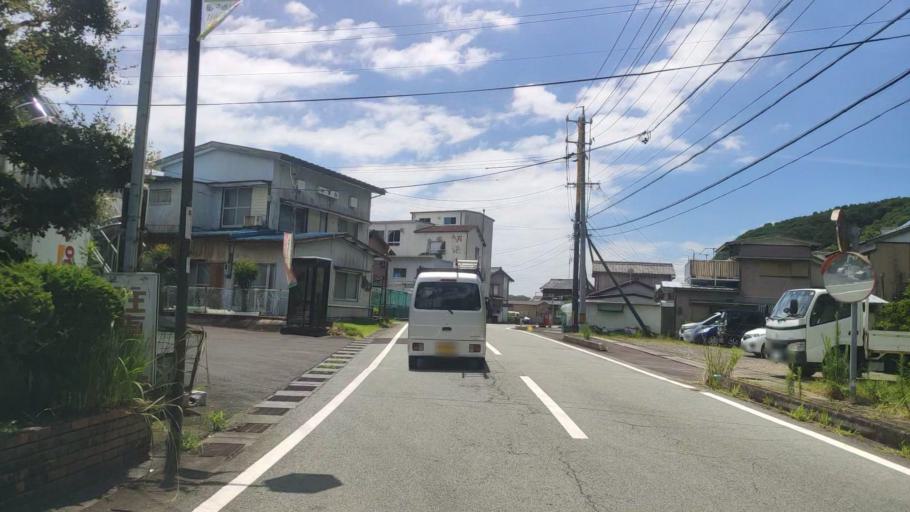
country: JP
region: Mie
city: Owase
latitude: 34.2111
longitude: 136.3510
